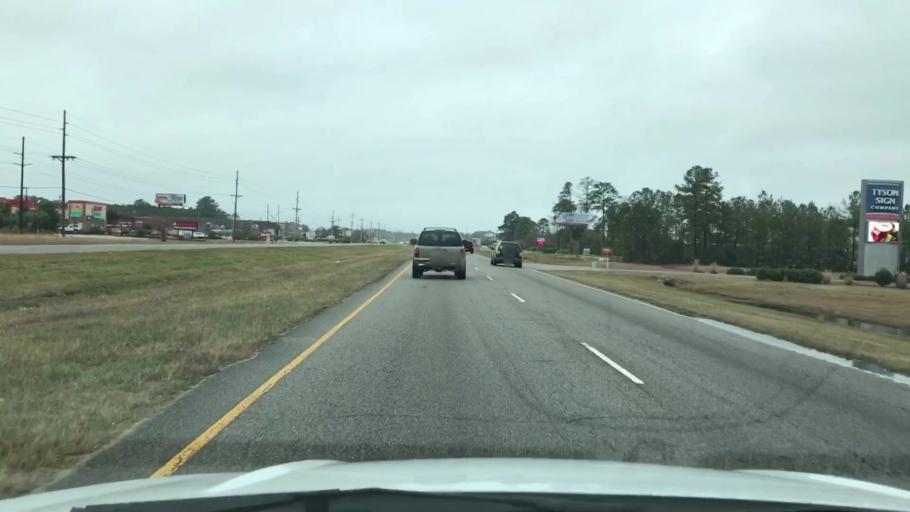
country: US
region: South Carolina
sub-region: Horry County
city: Red Hill
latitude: 33.7859
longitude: -78.9925
